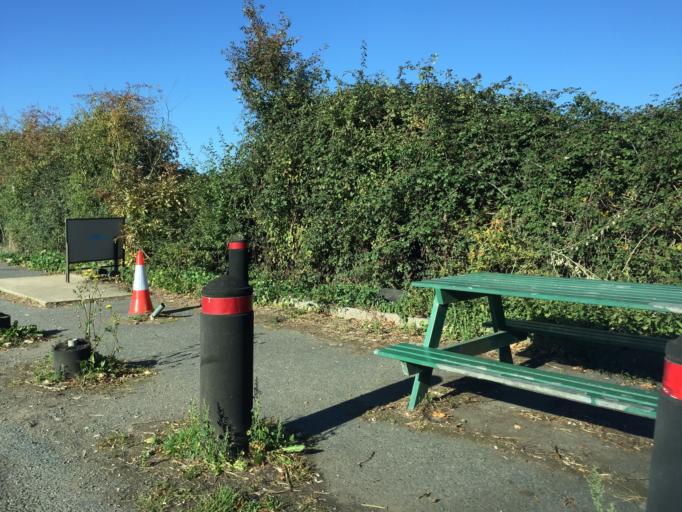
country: GB
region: England
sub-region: Gloucestershire
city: Stonehouse
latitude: 51.7572
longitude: -2.3186
